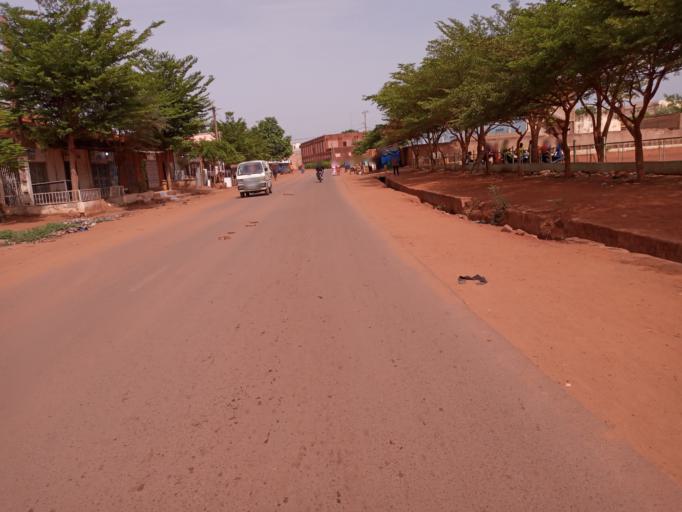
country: ML
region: Bamako
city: Bamako
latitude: 12.6099
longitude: -7.9551
